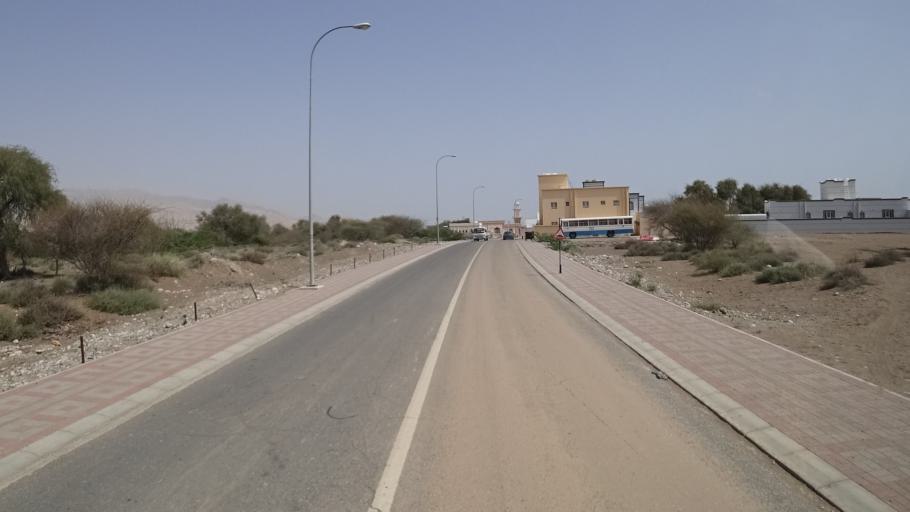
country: OM
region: Muhafazat Masqat
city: Muscat
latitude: 23.2365
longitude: 58.9101
